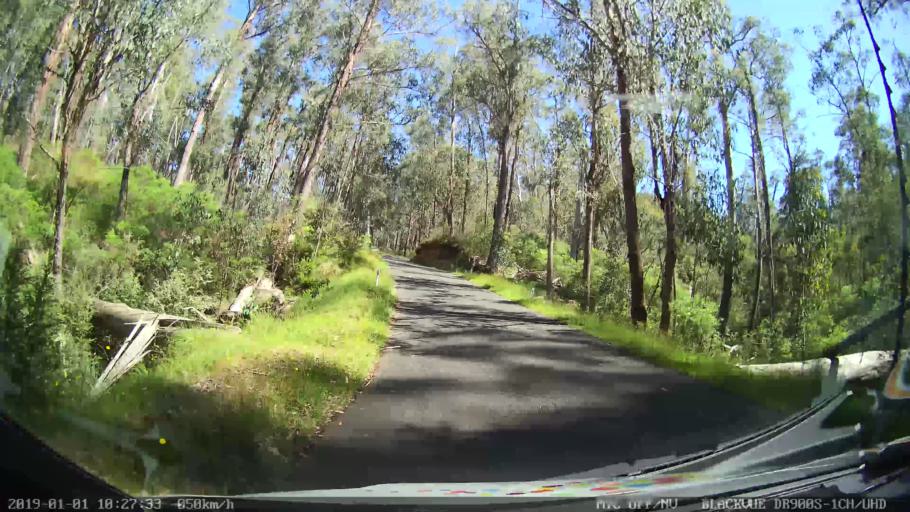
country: AU
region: New South Wales
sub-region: Snowy River
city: Jindabyne
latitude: -36.0655
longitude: 148.2374
